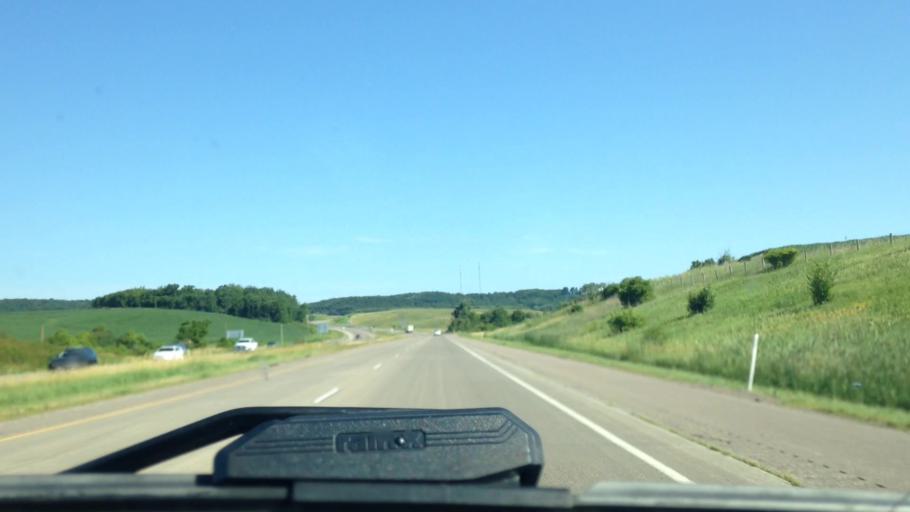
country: US
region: Wisconsin
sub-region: Trempealeau County
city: Osseo
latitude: 44.5923
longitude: -91.2145
